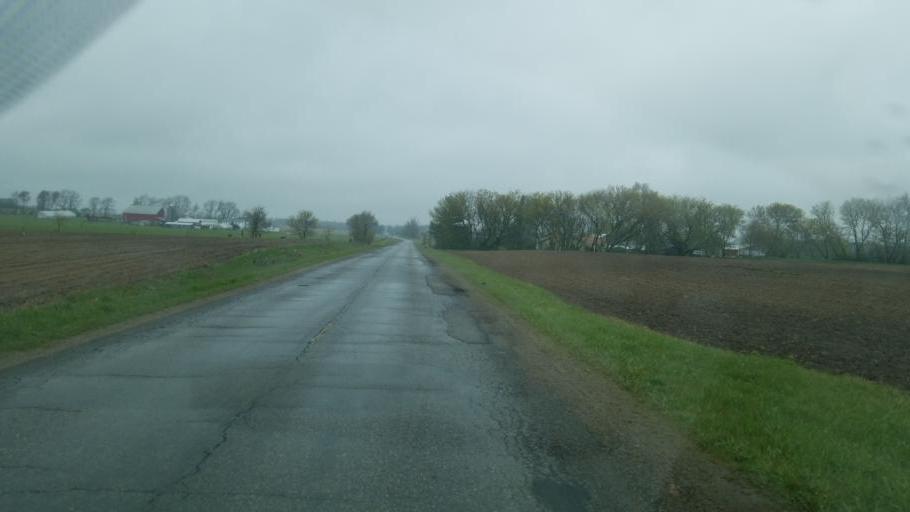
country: US
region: Michigan
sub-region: Mecosta County
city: Canadian Lakes
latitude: 43.5446
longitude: -85.3427
